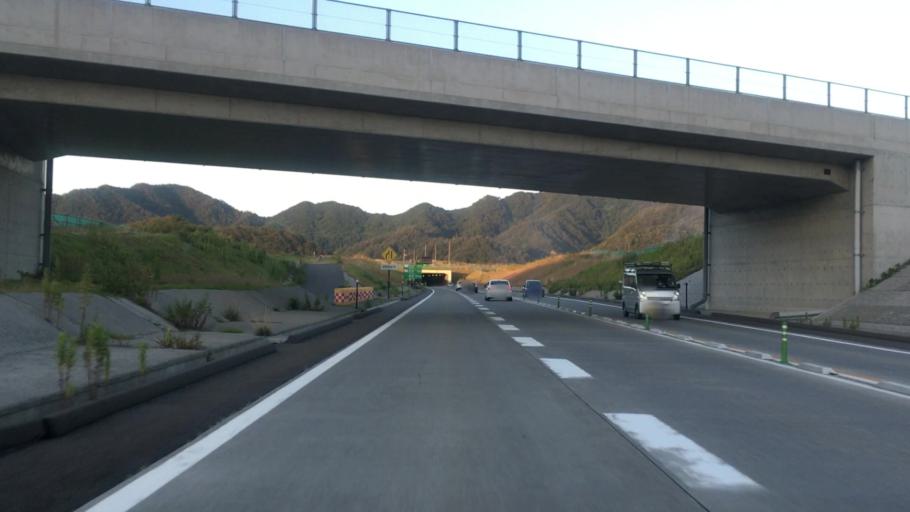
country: JP
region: Tottori
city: Tottori
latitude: 35.5503
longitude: 134.2714
